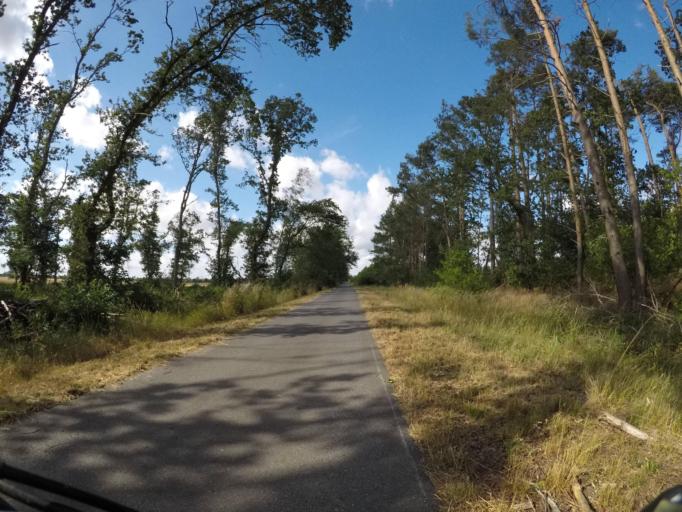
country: DE
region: Lower Saxony
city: Damnatz
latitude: 53.1757
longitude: 11.1691
